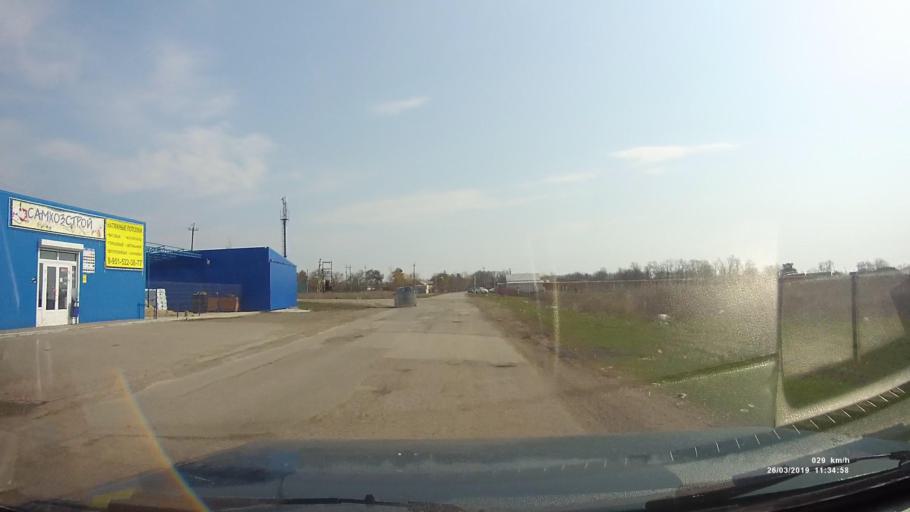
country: RU
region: Rostov
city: Novobessergenovka
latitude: 47.1472
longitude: 38.6347
